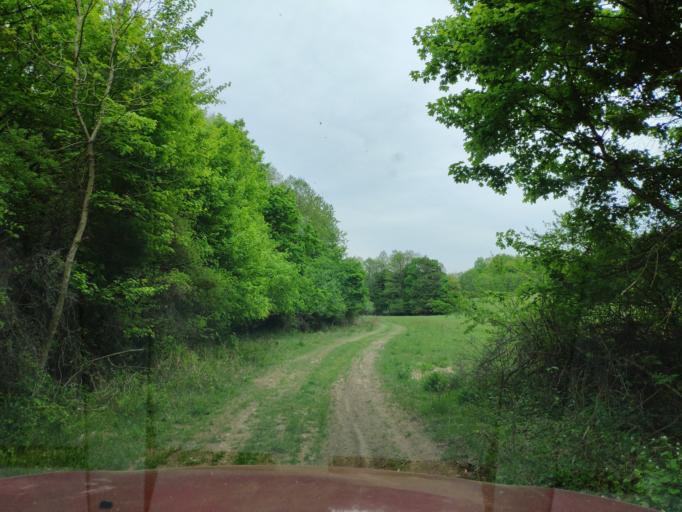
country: SK
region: Banskobystricky
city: Revuca
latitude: 48.5191
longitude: 20.1570
